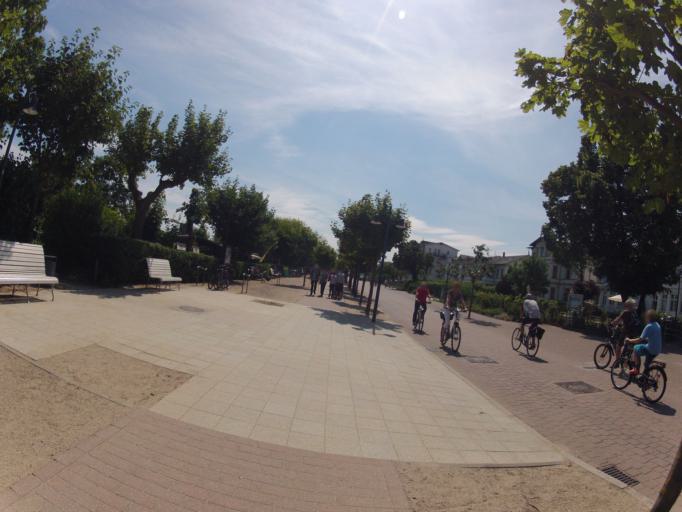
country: DE
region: Mecklenburg-Vorpommern
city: Seebad Heringsdorf
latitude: 53.9448
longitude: 14.1856
